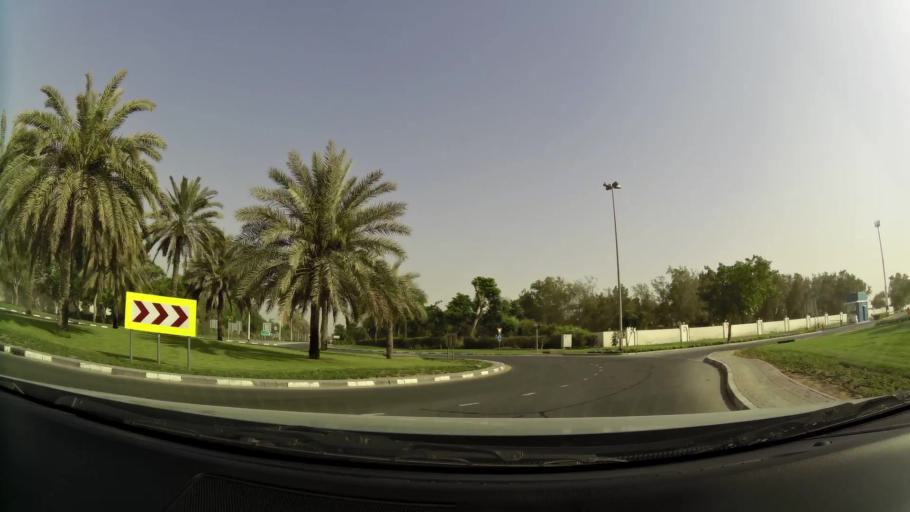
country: AE
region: Dubai
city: Dubai
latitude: 25.1590
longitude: 55.3244
